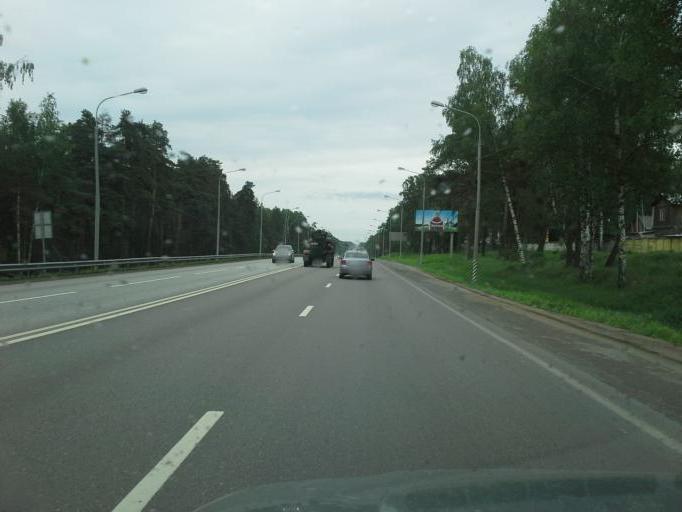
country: RU
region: Vladimir
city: Pokrov
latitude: 55.9206
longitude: 39.2112
